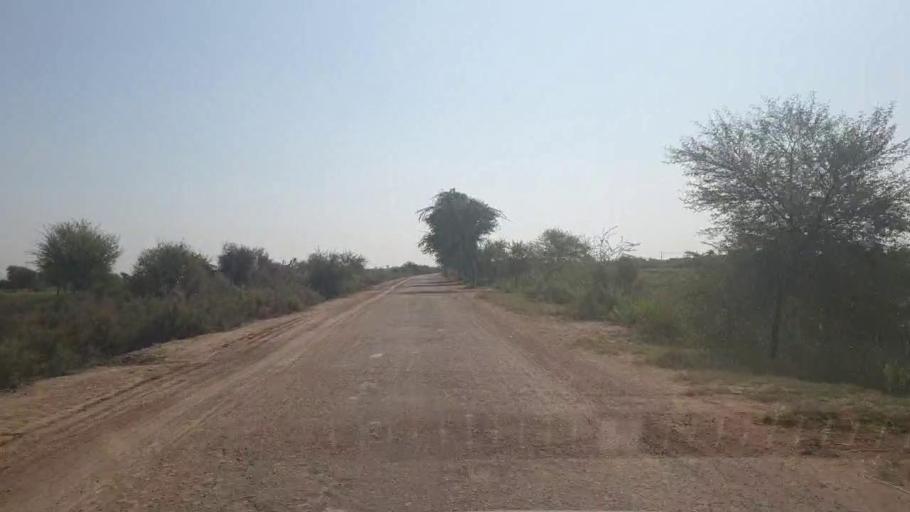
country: PK
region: Sindh
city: Badin
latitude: 24.5887
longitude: 68.8458
